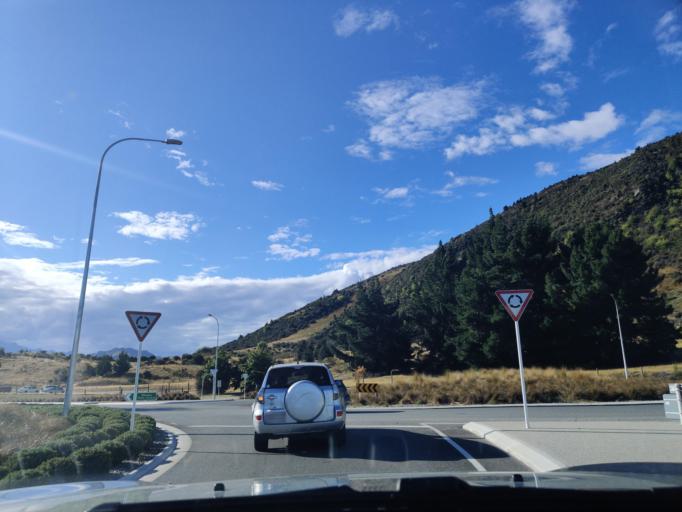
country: NZ
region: Otago
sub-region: Queenstown-Lakes District
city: Wanaka
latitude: -44.6948
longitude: 169.1563
